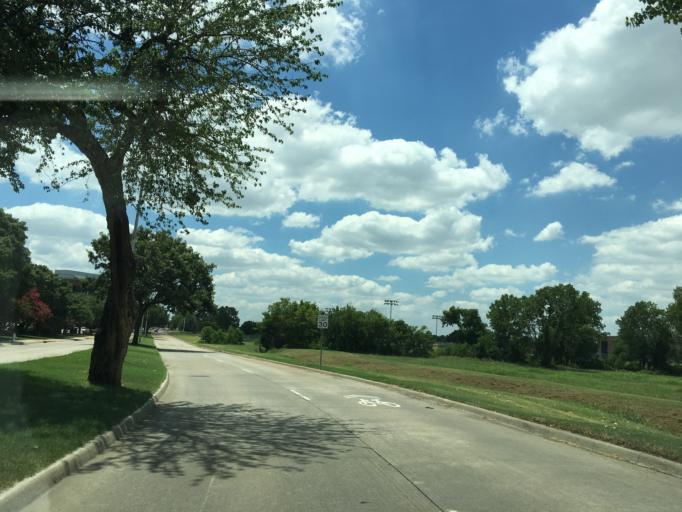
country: US
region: Texas
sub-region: Dallas County
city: Addison
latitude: 32.9318
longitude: -96.8444
